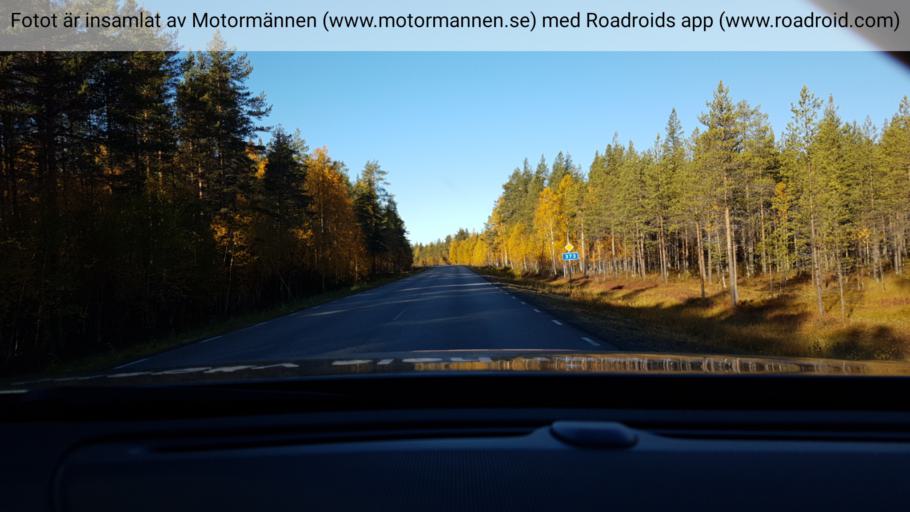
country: SE
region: Norrbotten
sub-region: Pitea Kommun
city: Roknas
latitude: 65.3421
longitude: 20.9579
